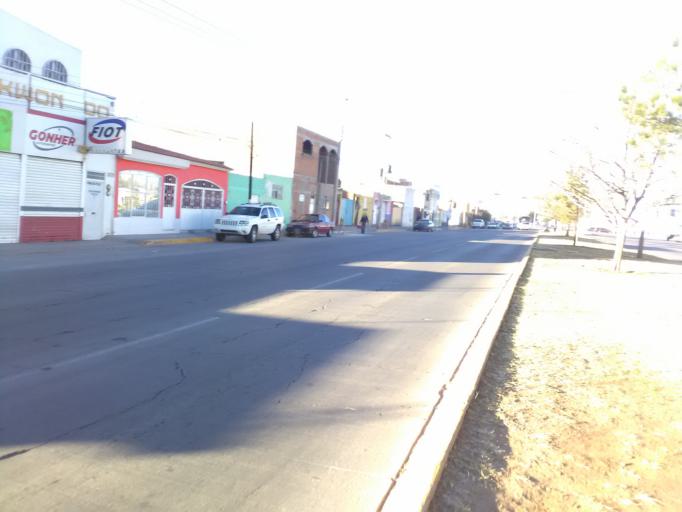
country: MX
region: Durango
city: Victoria de Durango
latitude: 24.0480
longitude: -104.6505
